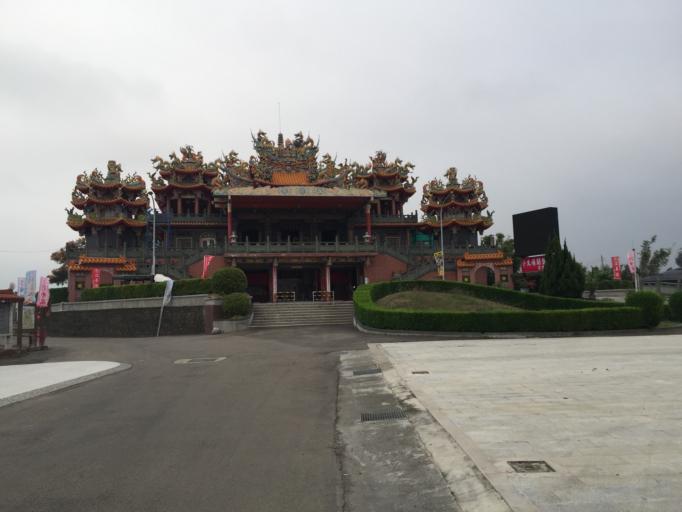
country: TW
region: Taiwan
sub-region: Miaoli
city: Miaoli
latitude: 24.5857
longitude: 120.8331
